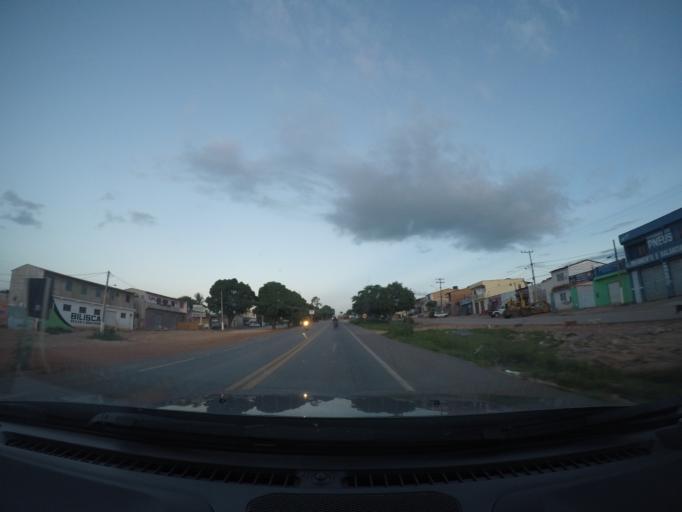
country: BR
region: Bahia
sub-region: Seabra
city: Seabra
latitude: -12.4282
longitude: -41.7754
